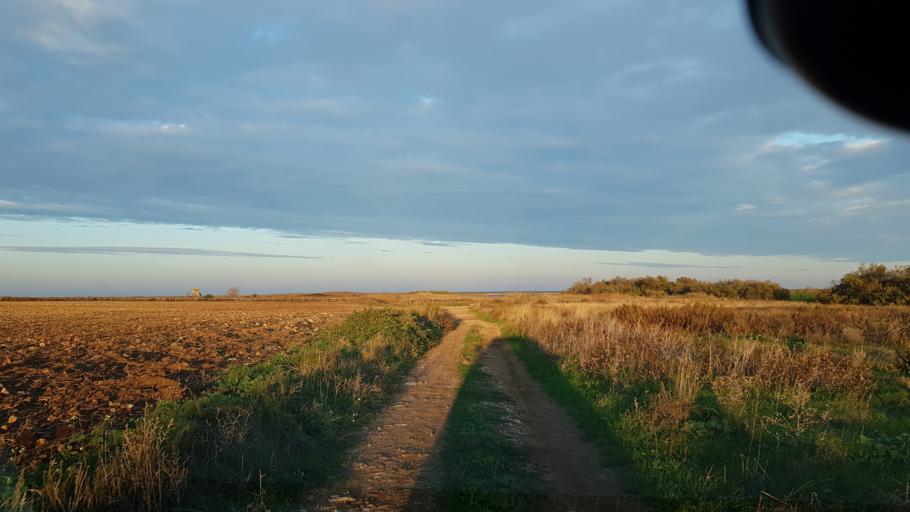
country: IT
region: Apulia
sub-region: Provincia di Brindisi
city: La Rosa
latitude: 40.6118
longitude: 18.0175
